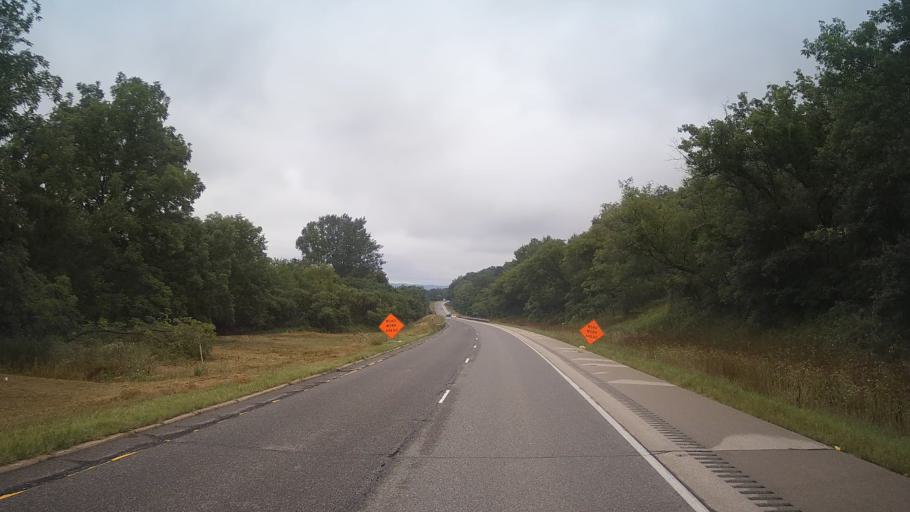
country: US
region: Wisconsin
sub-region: Trempealeau County
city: Trempealeau
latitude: 43.9214
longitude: -91.3955
